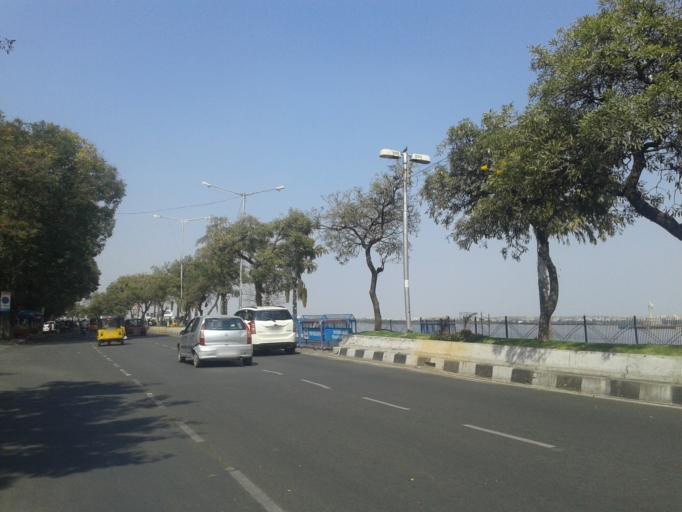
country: IN
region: Telangana
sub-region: Hyderabad
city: Hyderabad
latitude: 17.4111
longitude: 78.4713
